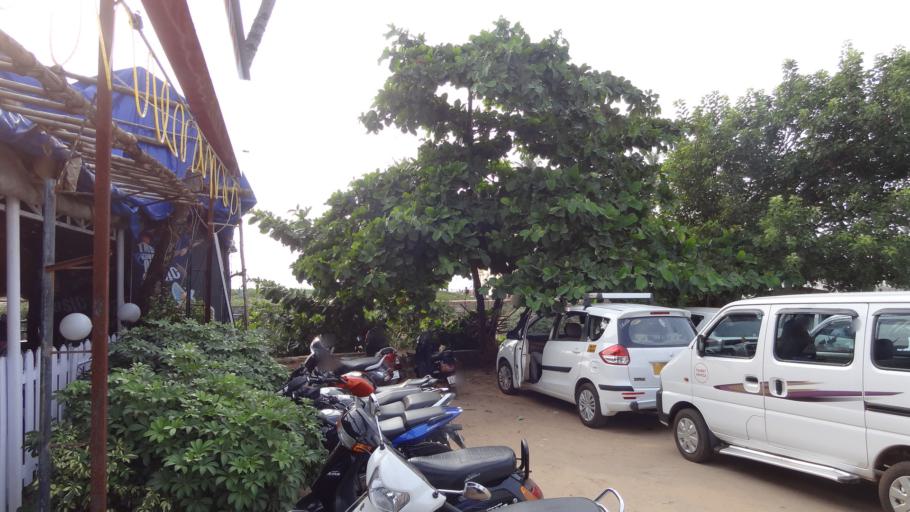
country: IN
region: Goa
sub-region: South Goa
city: Colva
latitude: 15.2759
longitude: 73.9145
